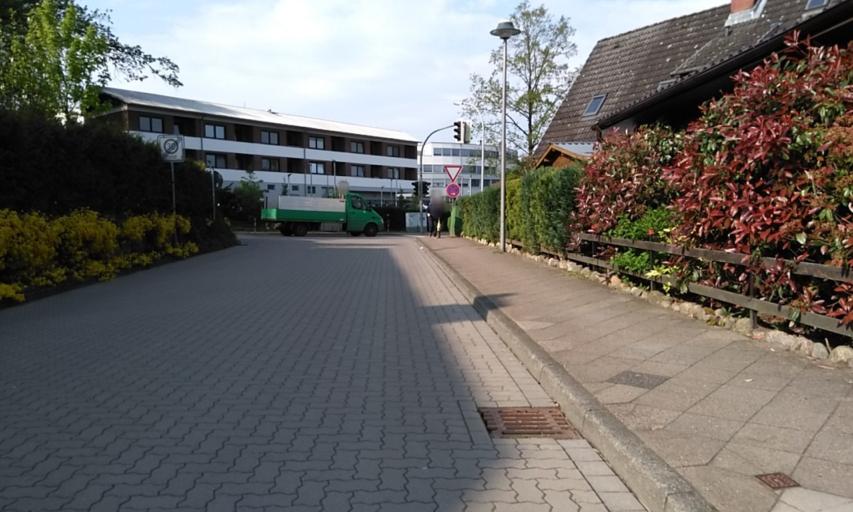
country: DE
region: Lower Saxony
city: Buxtehude
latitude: 53.4601
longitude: 9.6756
